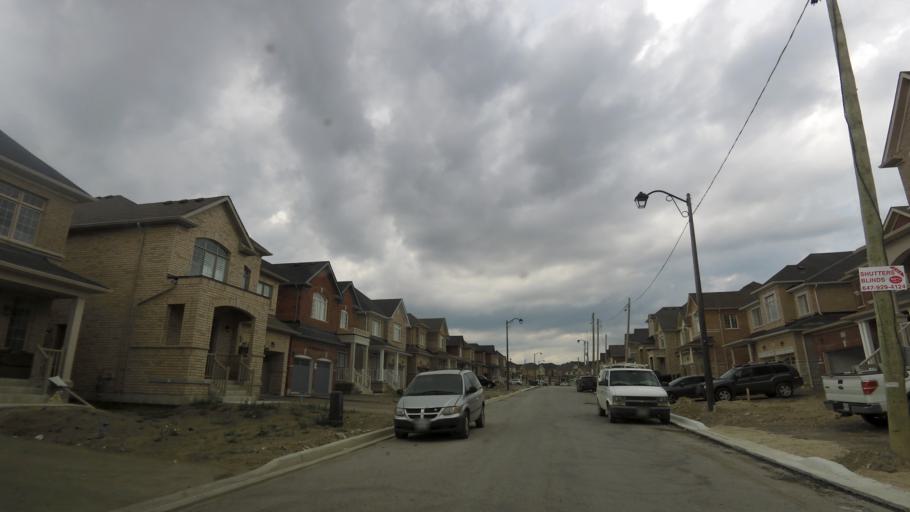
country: CA
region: Ontario
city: Brampton
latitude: 43.7521
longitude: -79.8388
